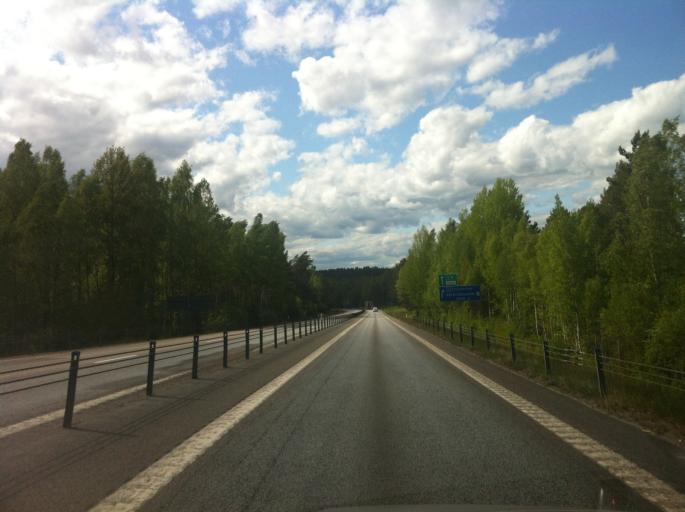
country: SE
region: Vaermland
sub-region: Kristinehamns Kommun
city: Kristinehamn
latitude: 59.3173
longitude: 14.1525
